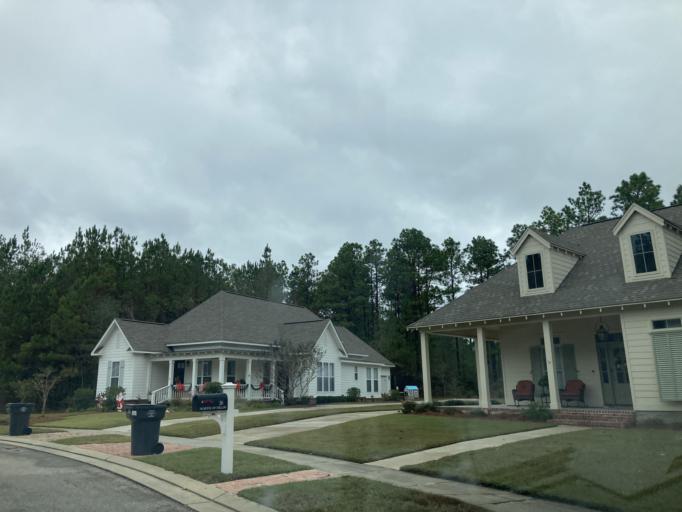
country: US
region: Mississippi
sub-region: Lamar County
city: West Hattiesburg
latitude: 31.2877
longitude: -89.4806
